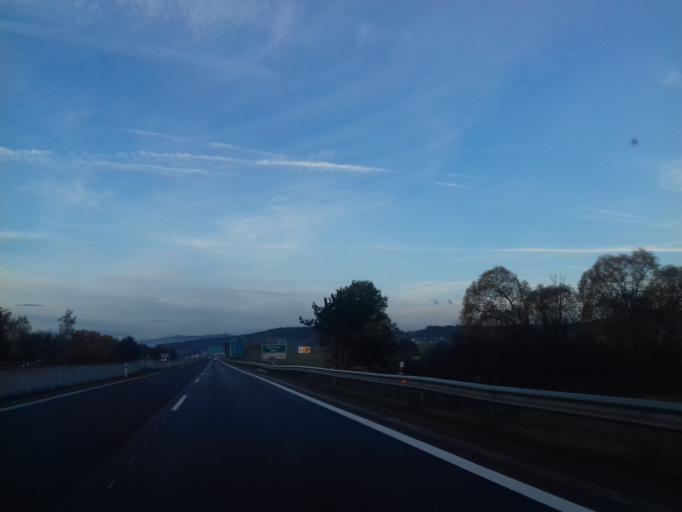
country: SK
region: Banskobystricky
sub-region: Okres Banska Bystrica
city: Zvolen
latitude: 48.6035
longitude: 19.1179
